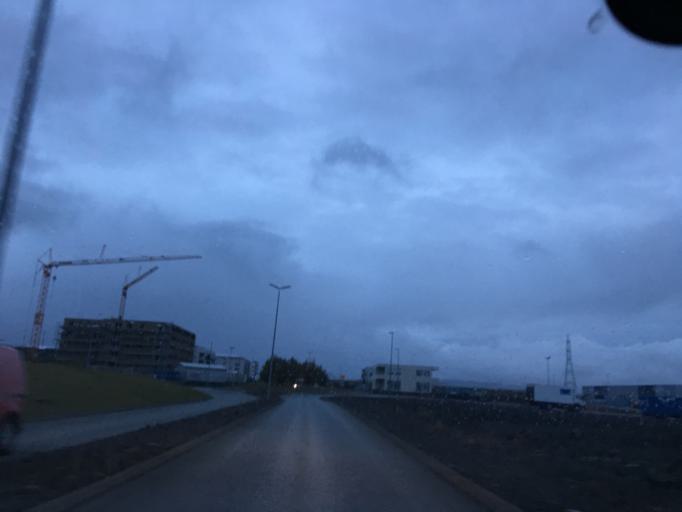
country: IS
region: Capital Region
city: Hafnarfjoerdur
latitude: 64.0452
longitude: -21.9823
